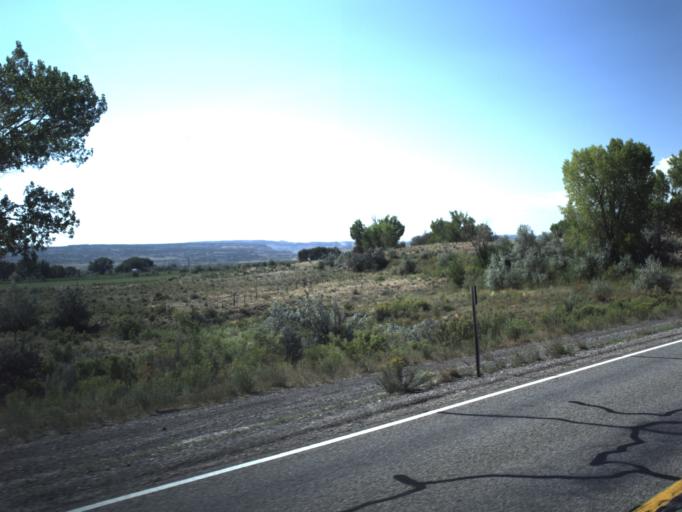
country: US
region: Utah
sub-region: Emery County
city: Ferron
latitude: 38.9123
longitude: -111.2668
